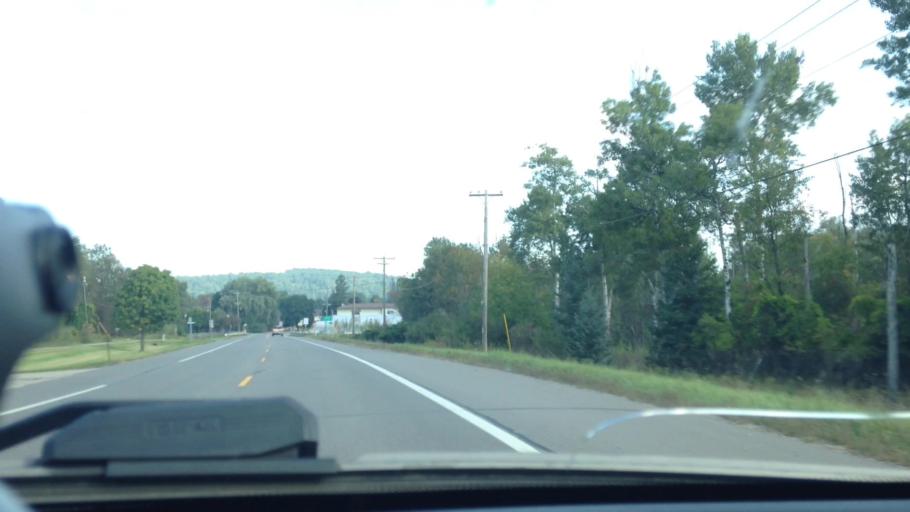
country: US
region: Michigan
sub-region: Dickinson County
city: Norway
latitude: 45.7784
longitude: -87.9091
